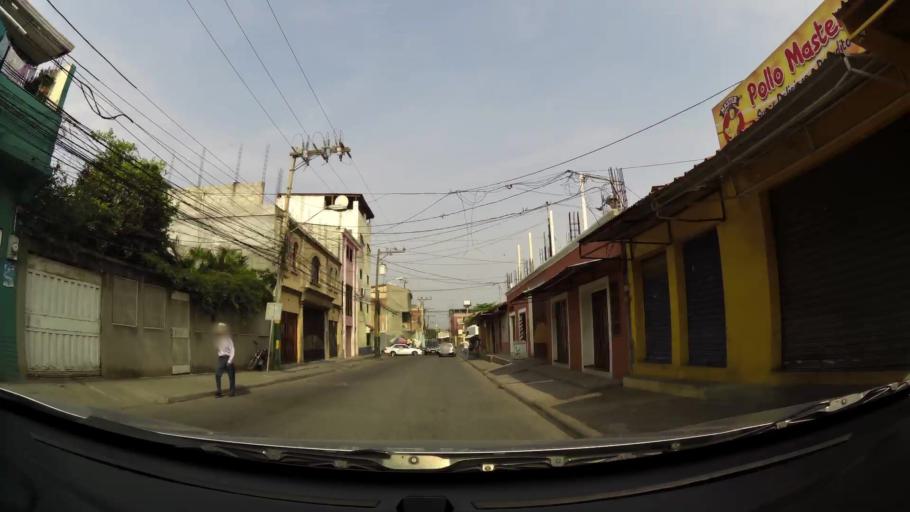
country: HN
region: Comayagua
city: Comayagua
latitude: 14.4562
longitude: -87.6401
